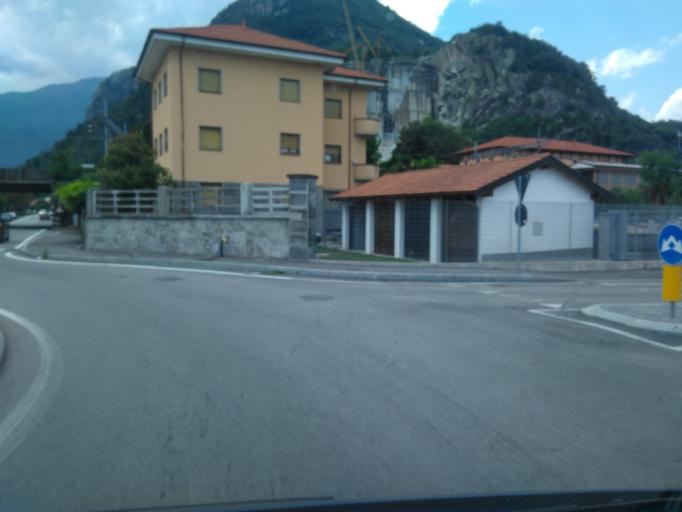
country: IT
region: Piedmont
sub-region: Provincia Verbano-Cusio-Ossola
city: Mergozzo
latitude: 45.9432
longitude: 8.4734
